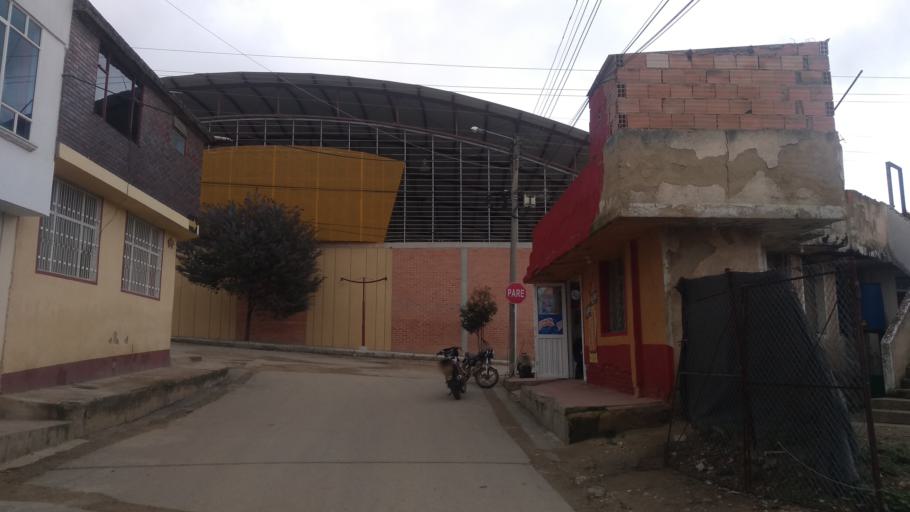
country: CO
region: Boyaca
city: Toca
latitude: 5.5624
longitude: -73.1839
